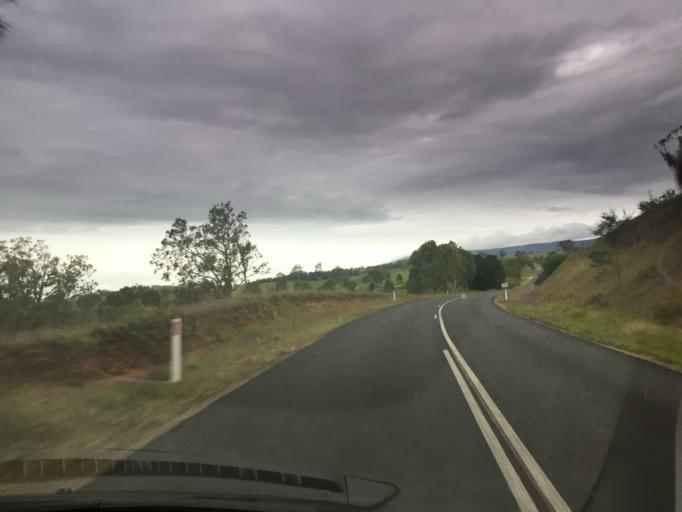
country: AU
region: New South Wales
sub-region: Bega Valley
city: Bega
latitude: -36.6592
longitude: 149.5833
